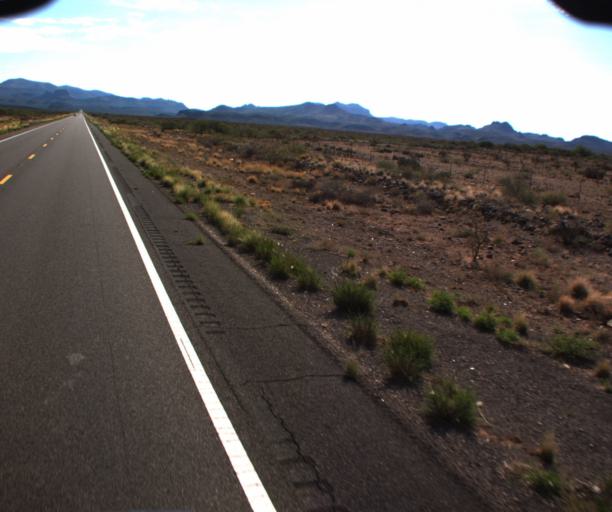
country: US
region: Arizona
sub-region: Graham County
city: Safford
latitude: 32.8224
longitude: -109.4717
